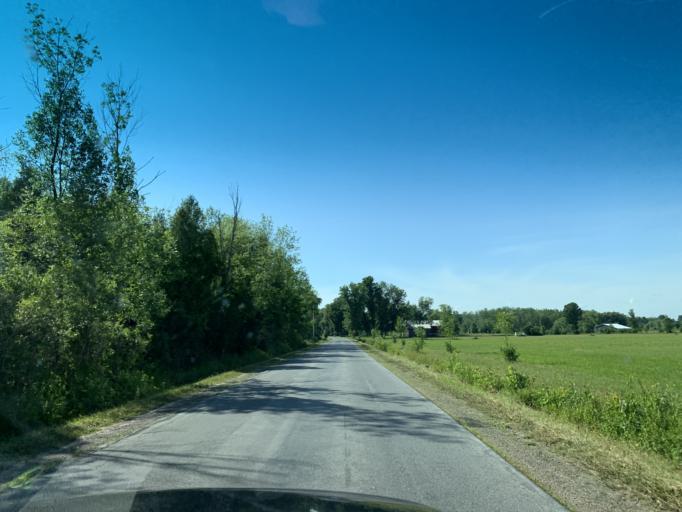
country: US
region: New York
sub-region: Madison County
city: Oneida
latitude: 43.1493
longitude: -75.6595
